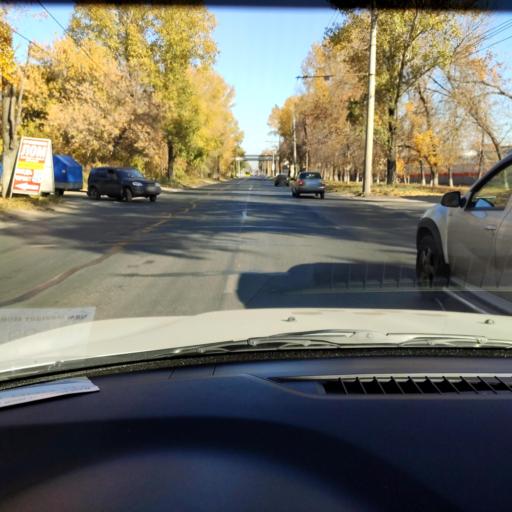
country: RU
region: Samara
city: Tol'yatti
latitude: 53.5491
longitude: 49.4479
